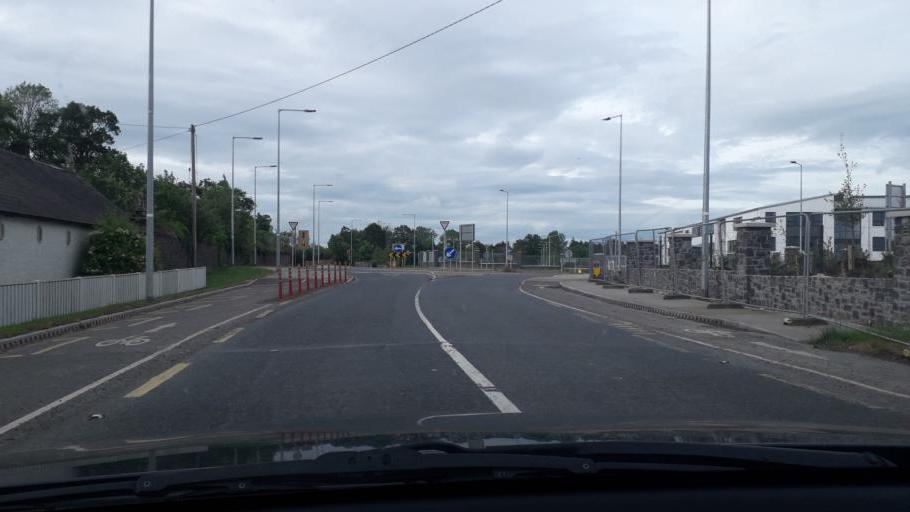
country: IE
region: Leinster
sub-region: County Carlow
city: Carlow
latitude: 52.8178
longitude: -6.9461
